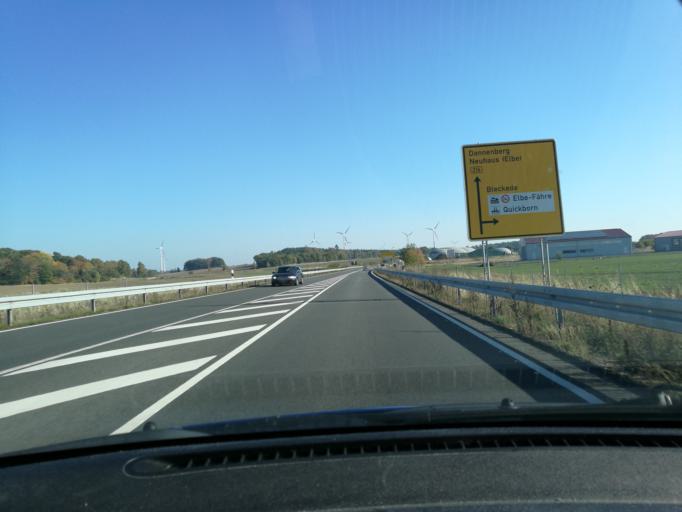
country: DE
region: Lower Saxony
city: Dahlem
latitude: 53.1951
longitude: 10.7451
